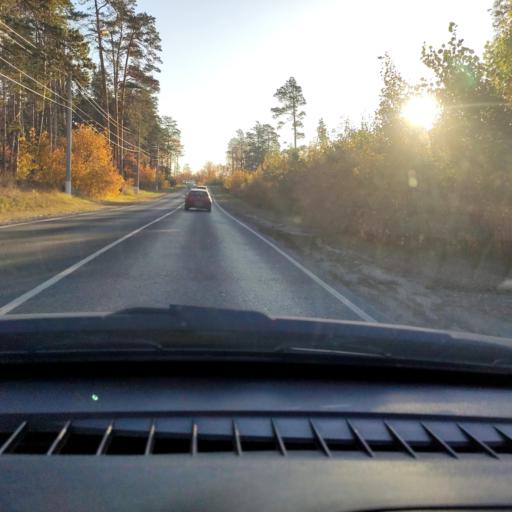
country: RU
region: Samara
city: Tol'yatti
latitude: 53.4733
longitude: 49.3834
